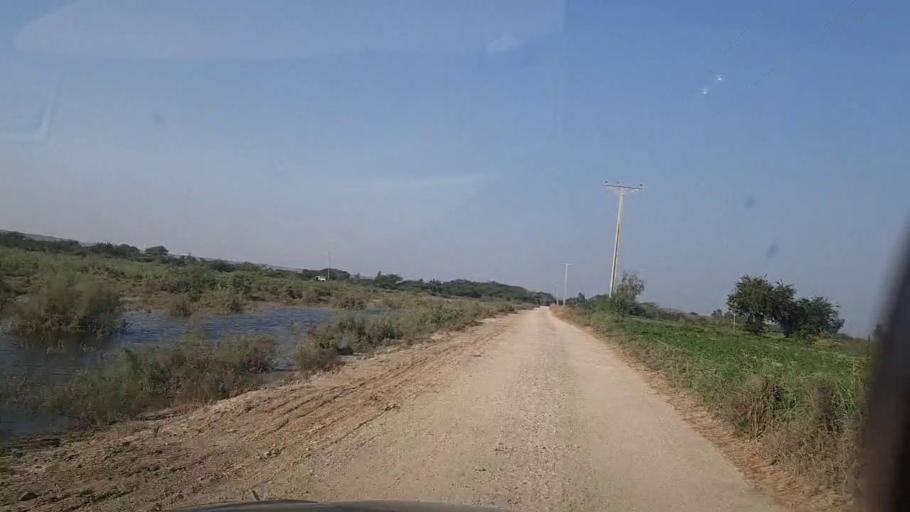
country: PK
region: Sindh
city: Thatta
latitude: 24.6060
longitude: 67.8745
